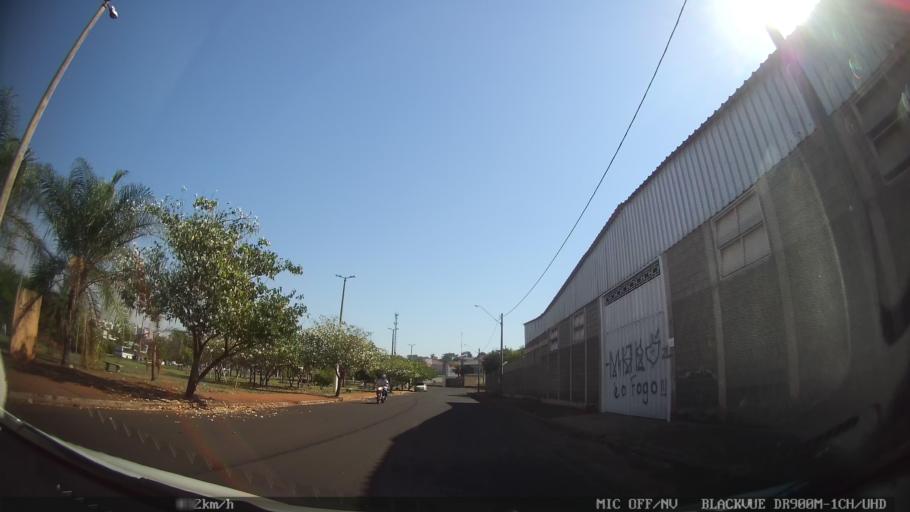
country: BR
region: Sao Paulo
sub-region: Ribeirao Preto
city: Ribeirao Preto
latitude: -21.2112
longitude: -47.7745
